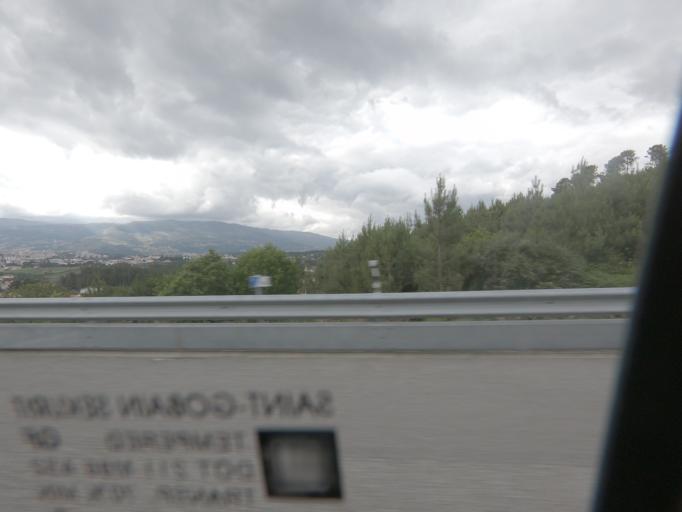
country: PT
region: Vila Real
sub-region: Vila Real
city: Vila Real
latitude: 41.2846
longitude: -7.7072
